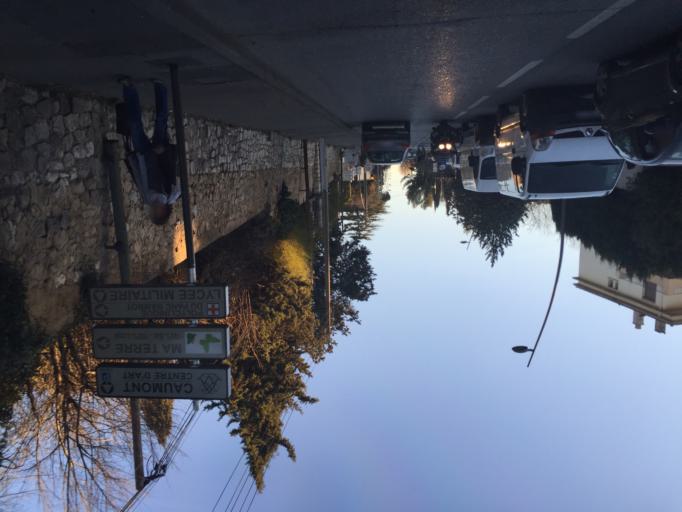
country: FR
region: Provence-Alpes-Cote d'Azur
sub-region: Departement des Bouches-du-Rhone
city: Aix-en-Provence
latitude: 43.5198
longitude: 5.4611
